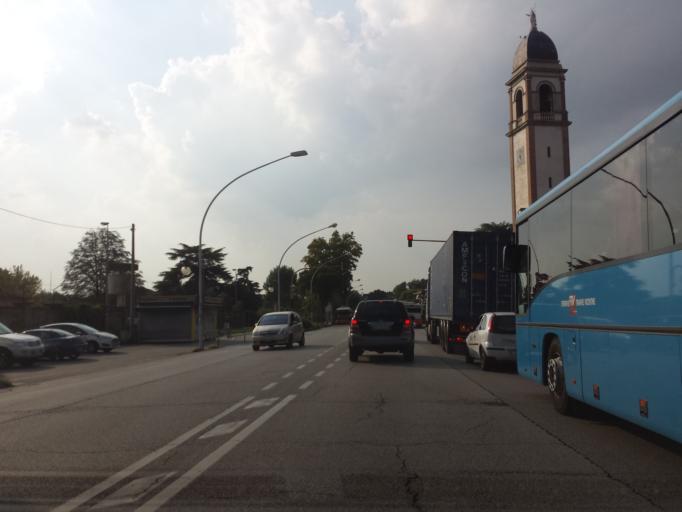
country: IT
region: Veneto
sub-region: Provincia di Padova
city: Caselle
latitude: 45.4141
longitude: 11.8367
